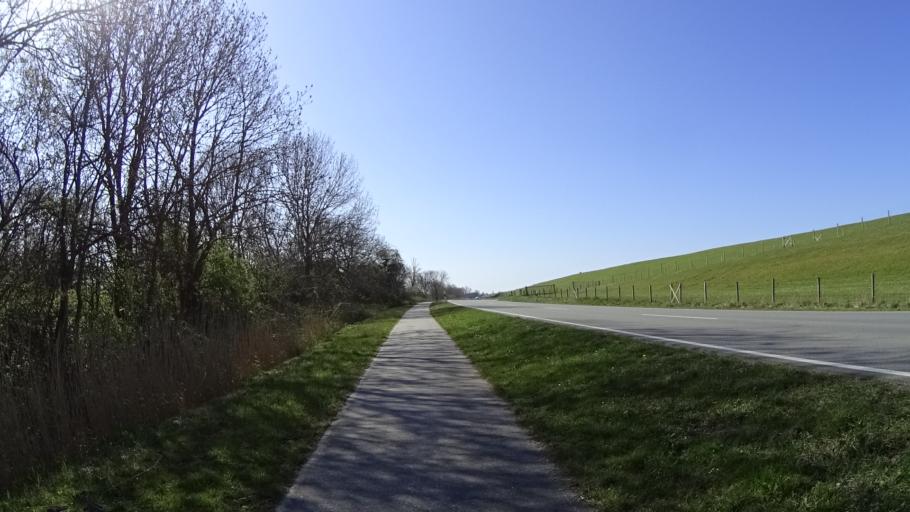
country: DE
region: Lower Saxony
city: Jemgum
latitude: 53.2717
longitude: 7.4077
